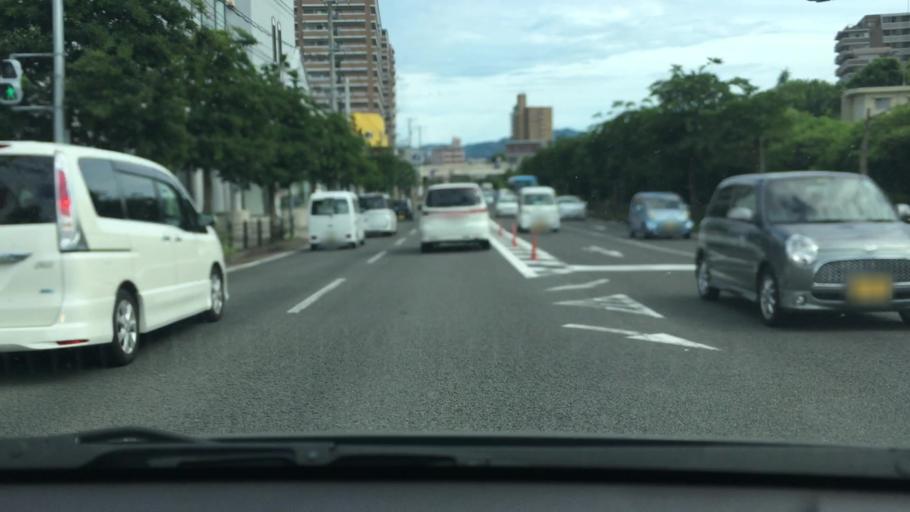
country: JP
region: Nagasaki
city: Obita
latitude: 32.7991
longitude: 129.8539
